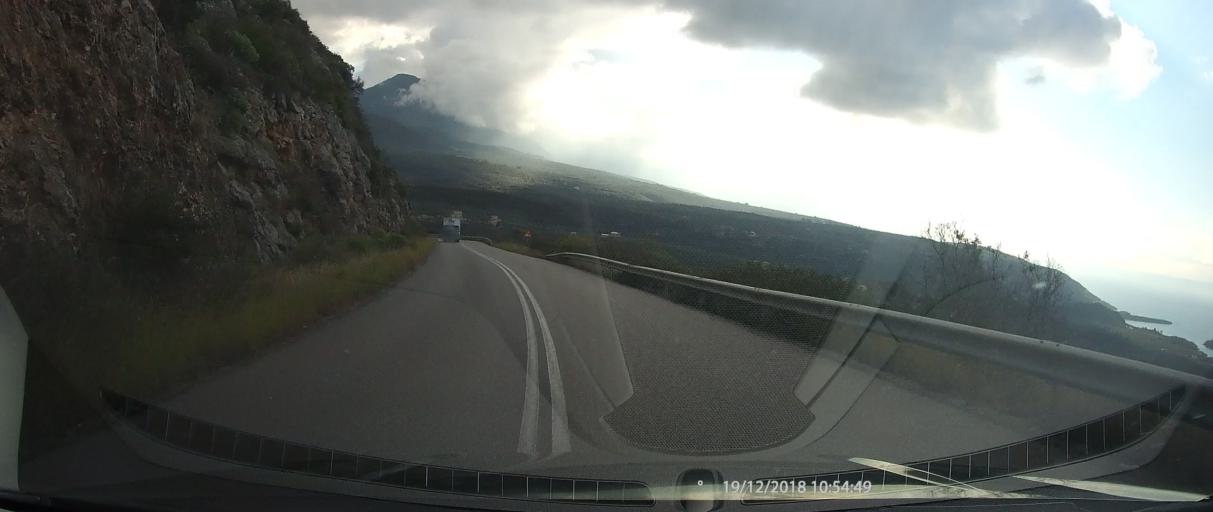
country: GR
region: Peloponnese
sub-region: Nomos Messinias
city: Kardamyli
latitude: 36.9053
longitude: 22.2361
